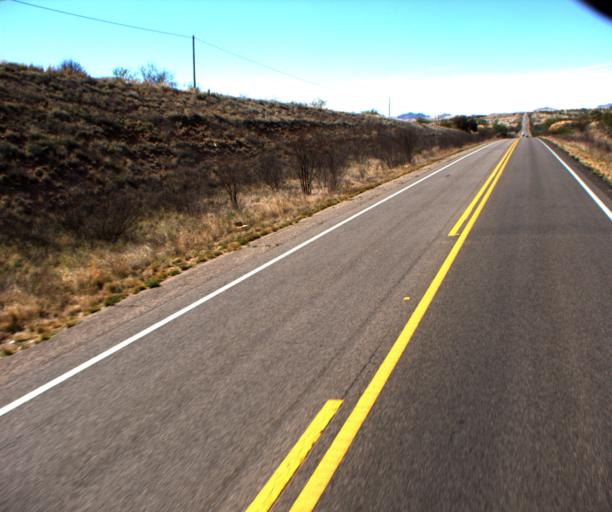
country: US
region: Arizona
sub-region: Pima County
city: Corona de Tucson
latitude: 31.7320
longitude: -110.6599
